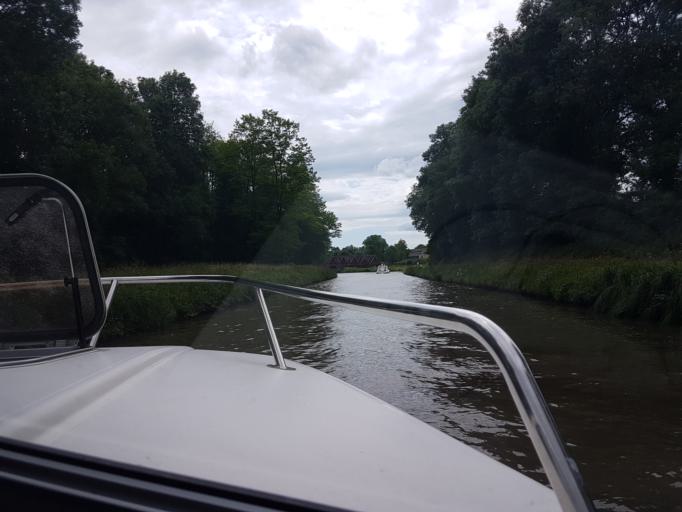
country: FR
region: Bourgogne
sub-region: Departement de la Nievre
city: Clamecy
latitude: 47.4805
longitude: 3.5242
